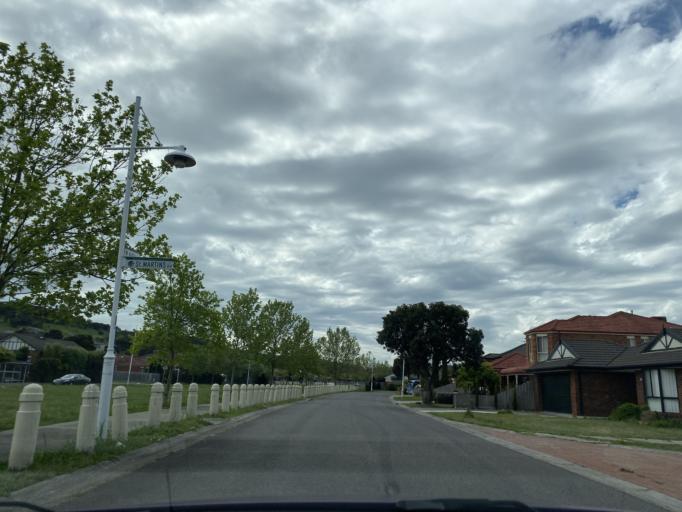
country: AU
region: Victoria
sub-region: Whittlesea
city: Mill Park
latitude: -37.6344
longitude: 145.0664
